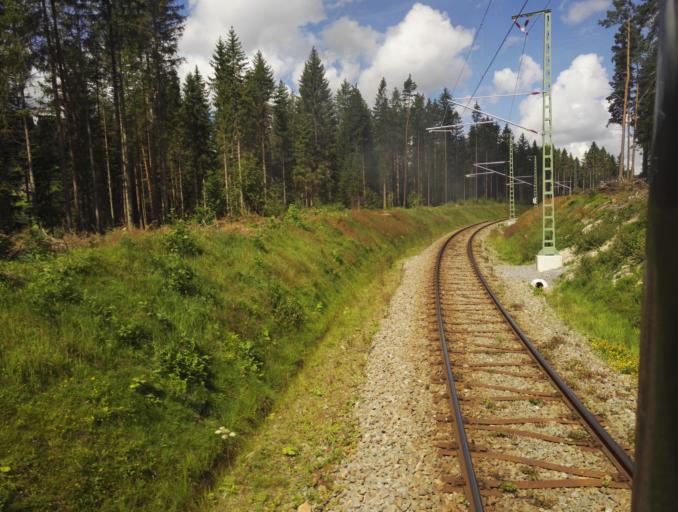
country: DE
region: Baden-Wuerttemberg
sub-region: Freiburg Region
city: Hinterzarten
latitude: 47.8618
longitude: 8.1084
